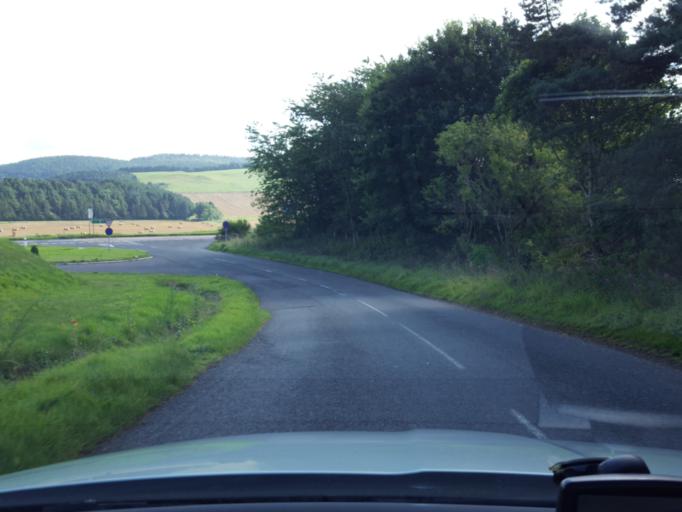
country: GB
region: Scotland
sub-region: Fife
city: Newport-On-Tay
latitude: 56.4056
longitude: -2.9588
